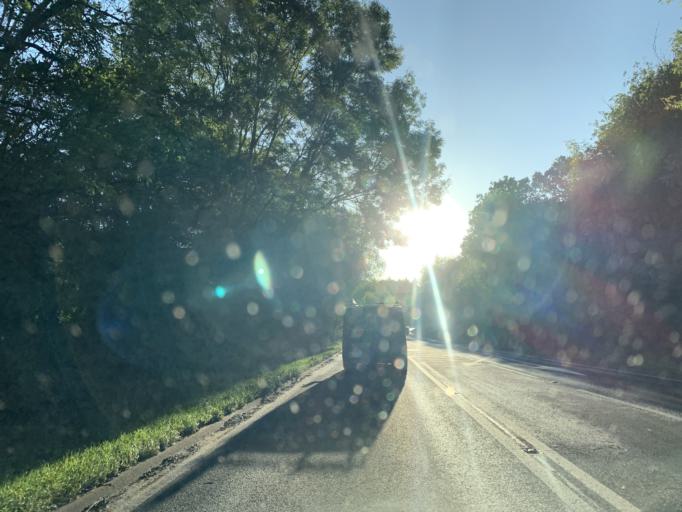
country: GB
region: England
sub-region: Wiltshire
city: Whiteparish
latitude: 50.9961
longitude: -1.6524
